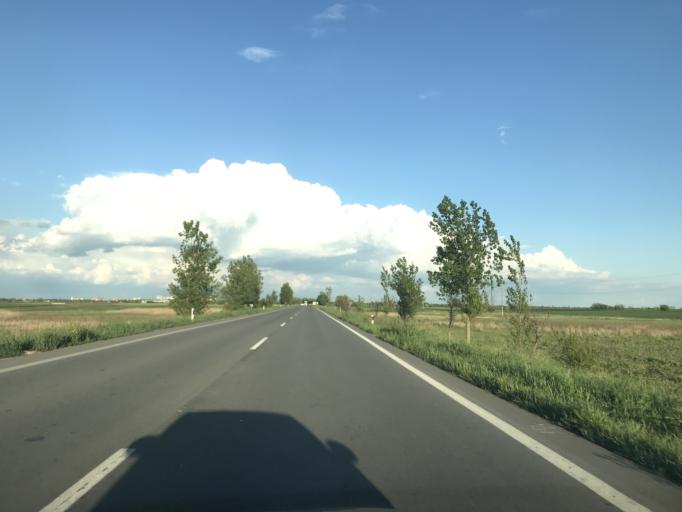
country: RS
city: Aradac
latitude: 45.3842
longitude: 20.3261
